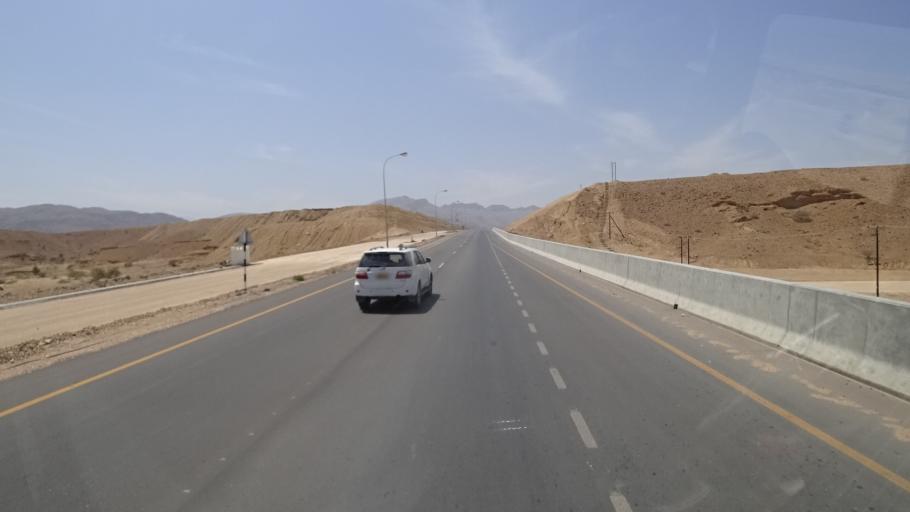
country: OM
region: Ash Sharqiyah
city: Sur
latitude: 22.5802
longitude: 59.4536
